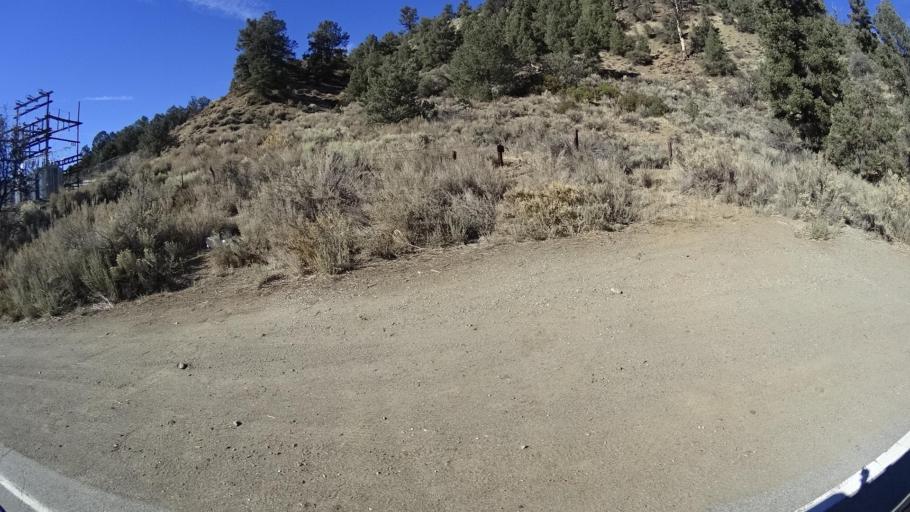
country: US
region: California
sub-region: Kern County
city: Frazier Park
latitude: 34.8153
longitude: -119.0094
